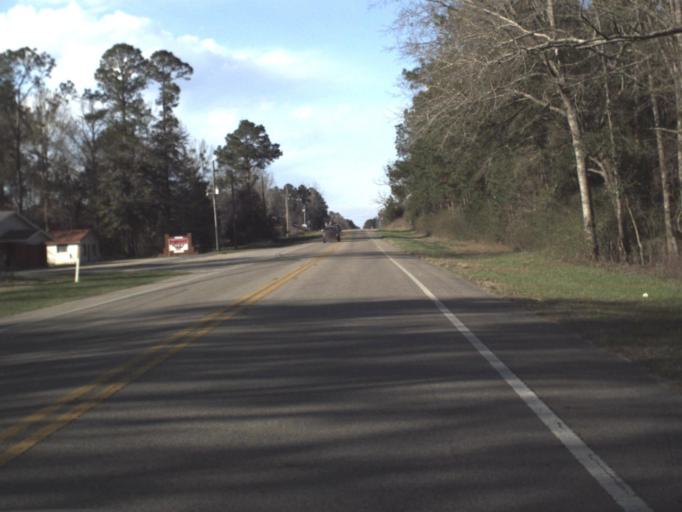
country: US
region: Florida
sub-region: Jackson County
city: Marianna
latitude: 30.7212
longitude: -85.2305
